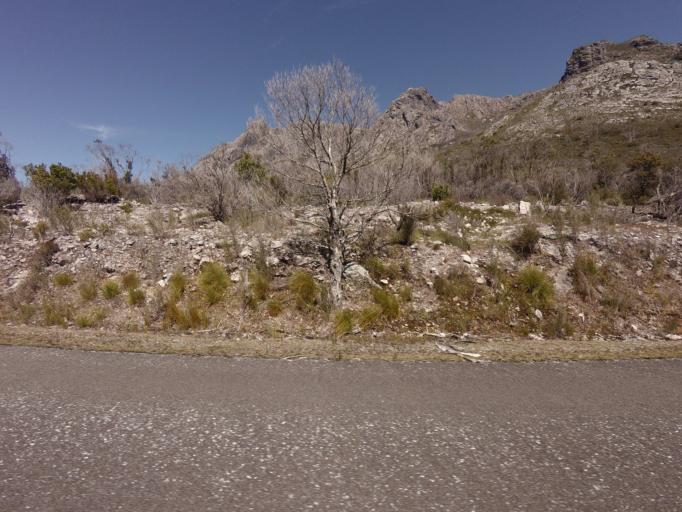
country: AU
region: Tasmania
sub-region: Huon Valley
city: Geeveston
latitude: -42.8609
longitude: 146.2249
